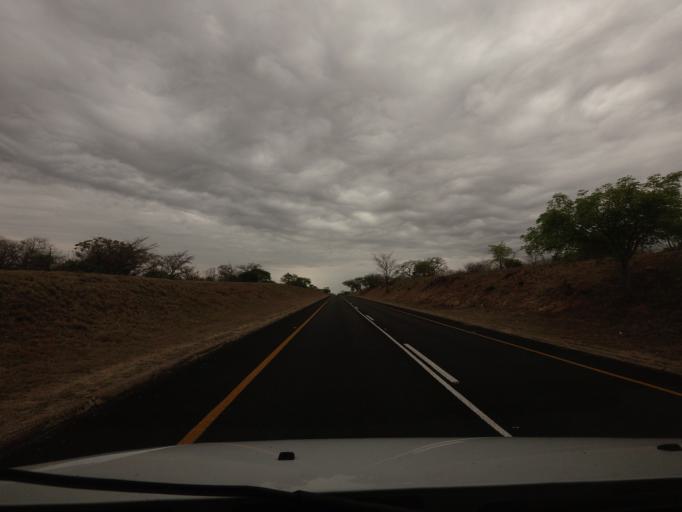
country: ZA
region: Limpopo
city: Thulamahashi
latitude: -24.5675
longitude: 31.0888
